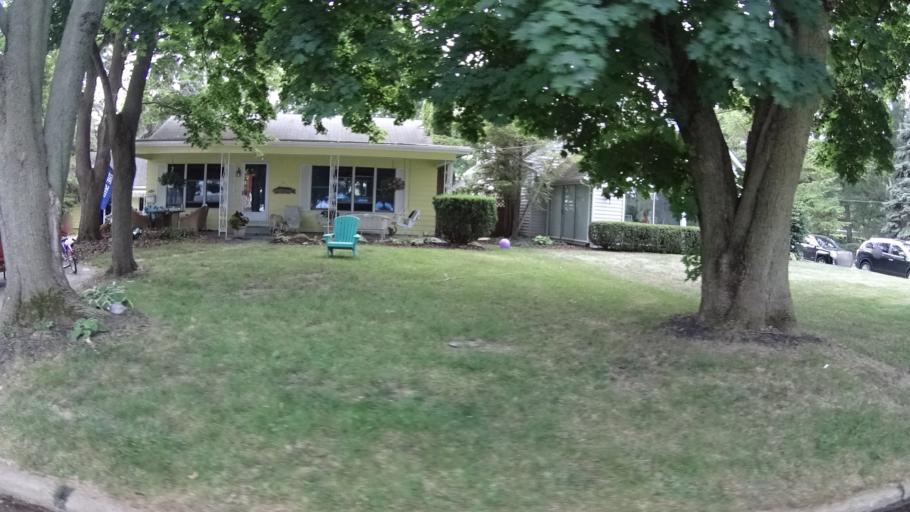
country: US
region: Ohio
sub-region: Erie County
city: Huron
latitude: 41.3928
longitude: -82.5390
